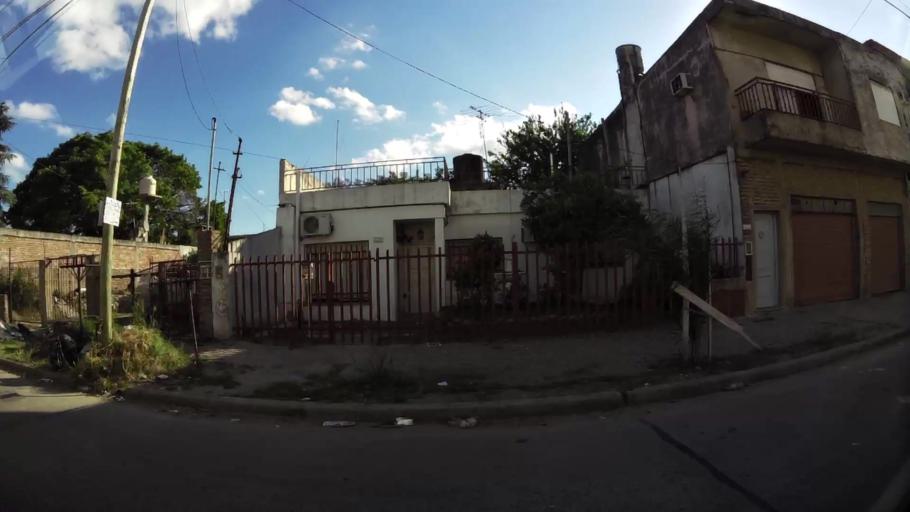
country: AR
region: Buenos Aires
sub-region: Partido de Moron
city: Moron
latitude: -34.6884
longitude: -58.6025
